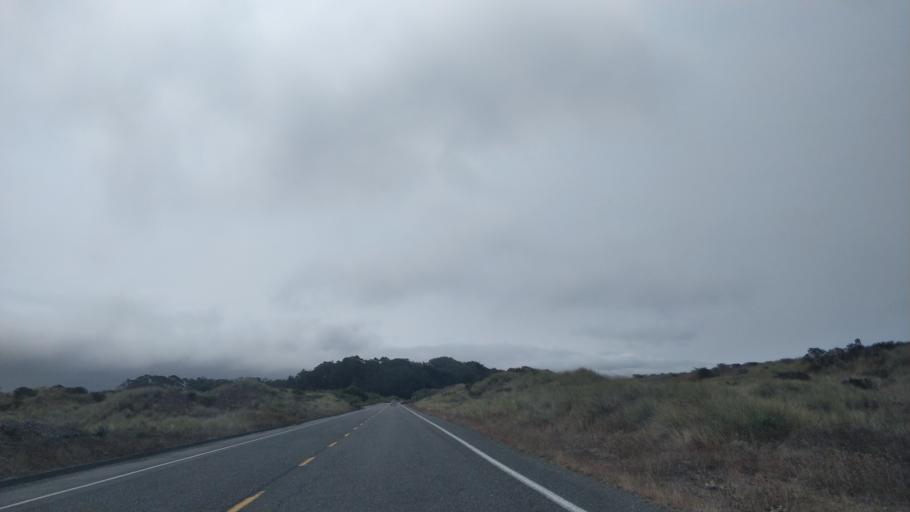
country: US
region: California
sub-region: Humboldt County
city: Bayview
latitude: 40.7850
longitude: -124.2069
